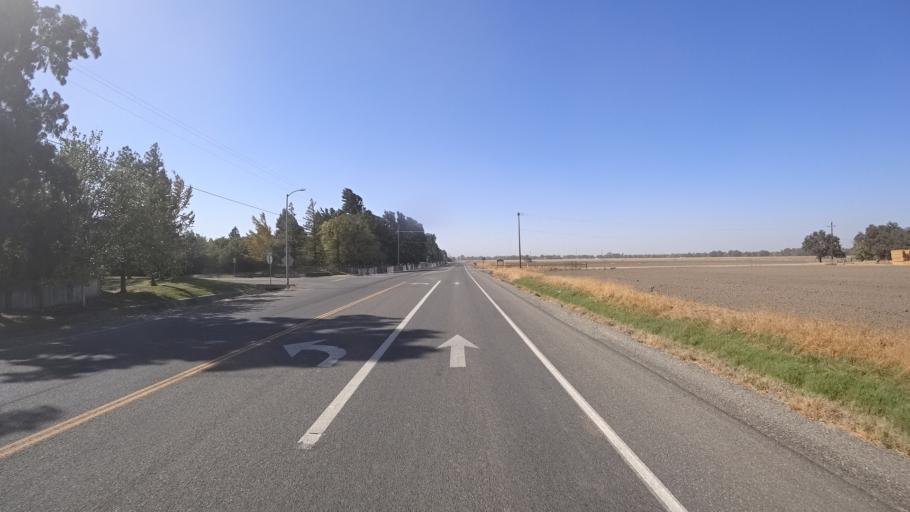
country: US
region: California
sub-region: Yolo County
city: Davis
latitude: 38.5902
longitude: -121.7721
